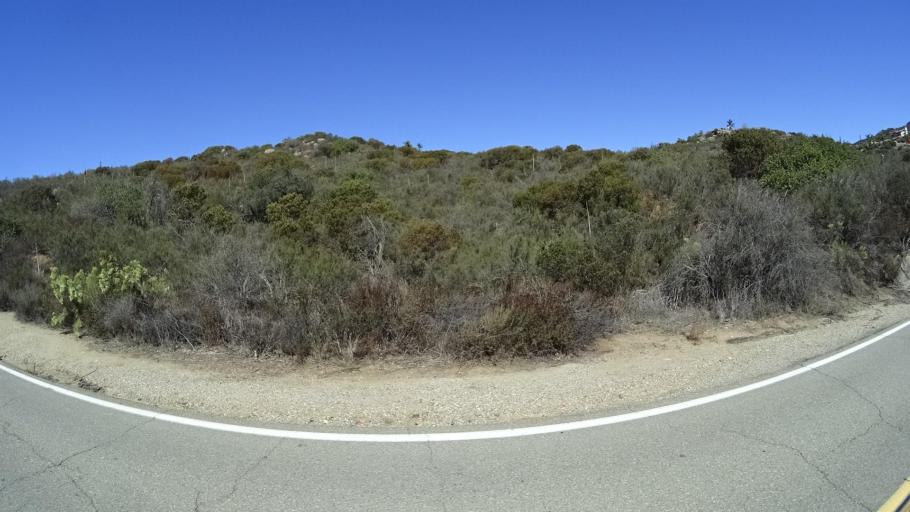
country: US
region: California
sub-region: San Diego County
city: Alpine
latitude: 32.8023
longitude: -116.7675
